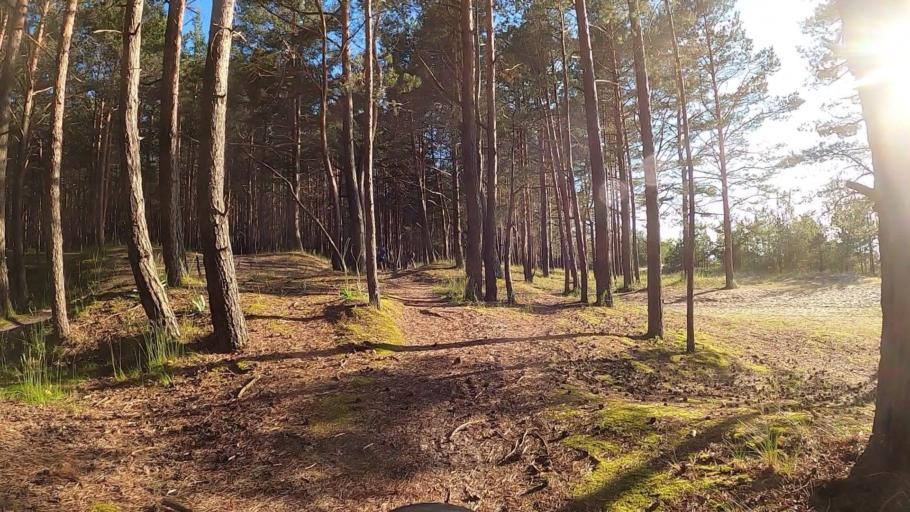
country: LV
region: Riga
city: Jaunciems
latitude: 57.1155
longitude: 24.1950
